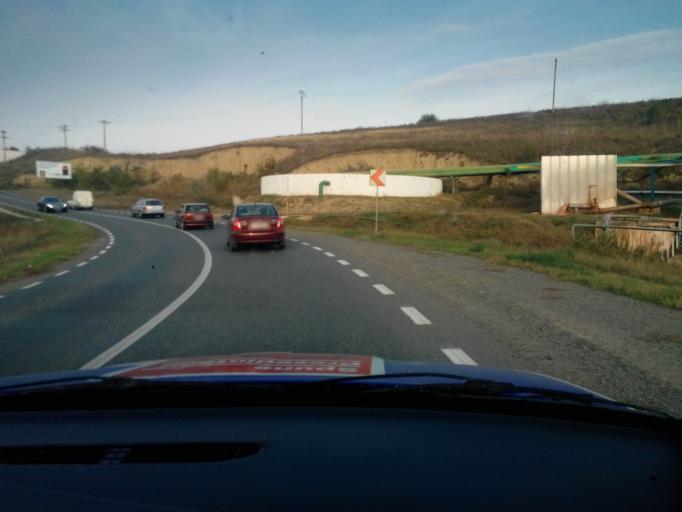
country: RO
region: Tulcea
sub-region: Comuna Somova
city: Mineri
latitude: 45.1662
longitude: 28.7335
